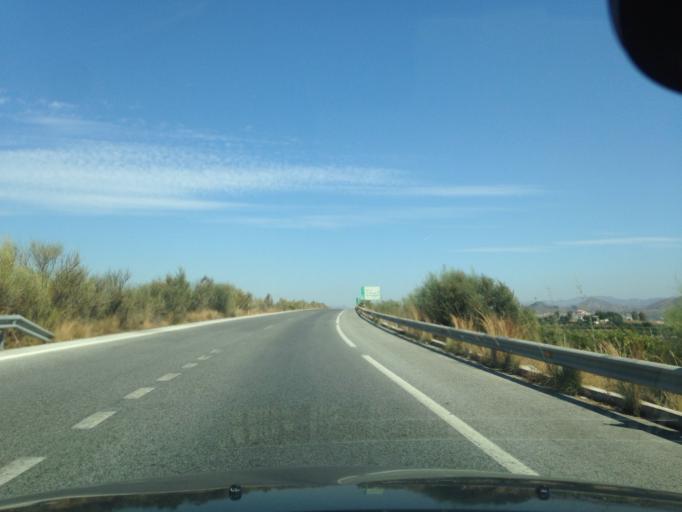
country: ES
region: Andalusia
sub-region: Provincia de Malaga
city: Alhaurin de la Torre
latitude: 36.7187
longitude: -4.5555
